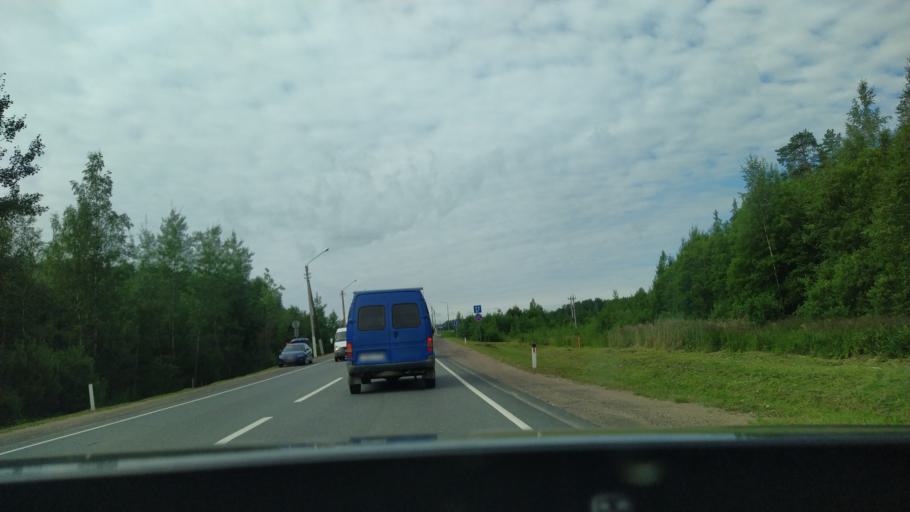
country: RU
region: Leningrad
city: Ul'yanovka
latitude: 59.6087
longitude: 30.7656
